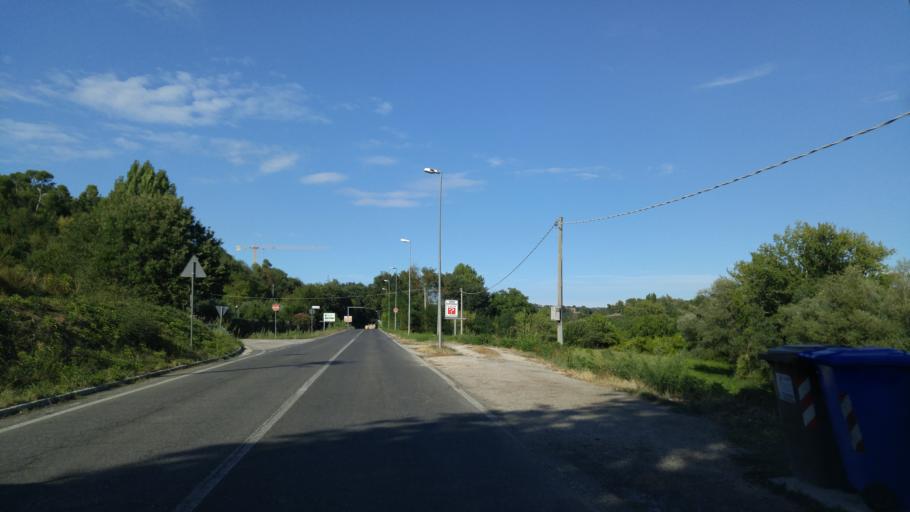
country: IT
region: The Marches
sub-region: Provincia di Pesaro e Urbino
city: Pesaro
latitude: 43.8781
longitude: 12.8961
